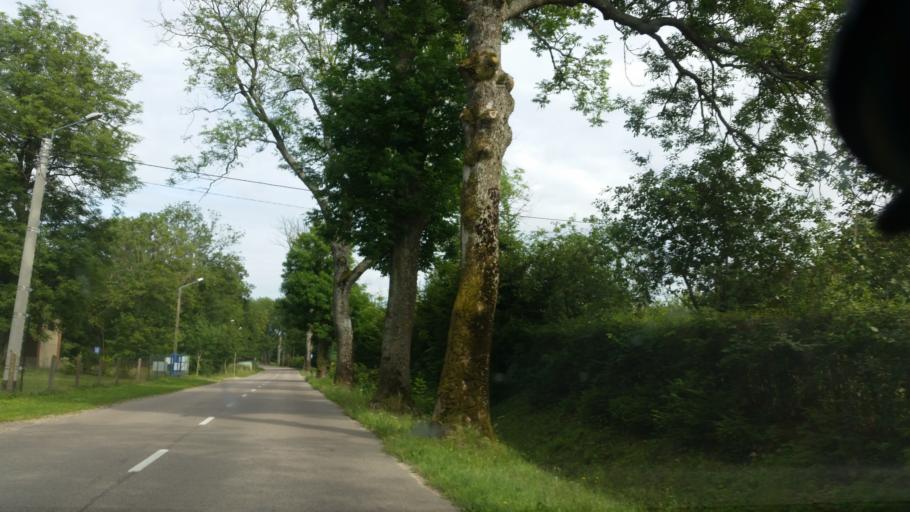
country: PL
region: Pomeranian Voivodeship
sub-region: Powiat wejherowski
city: Choczewo
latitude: 54.7224
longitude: 17.8879
